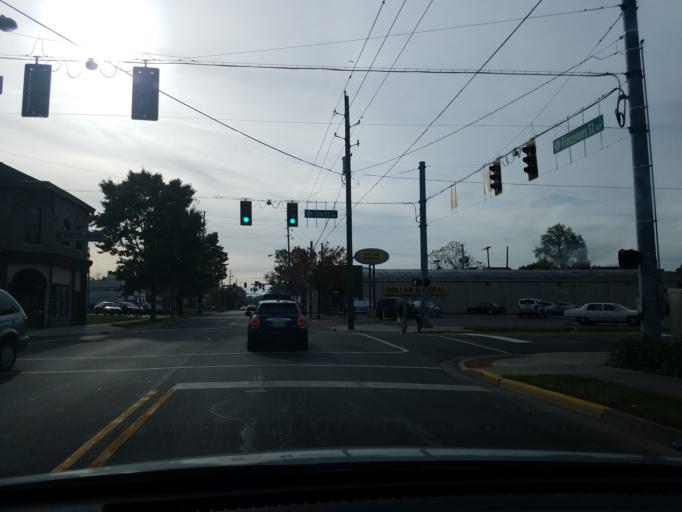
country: US
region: Indiana
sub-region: Floyd County
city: New Albany
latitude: 38.2938
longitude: -85.8082
